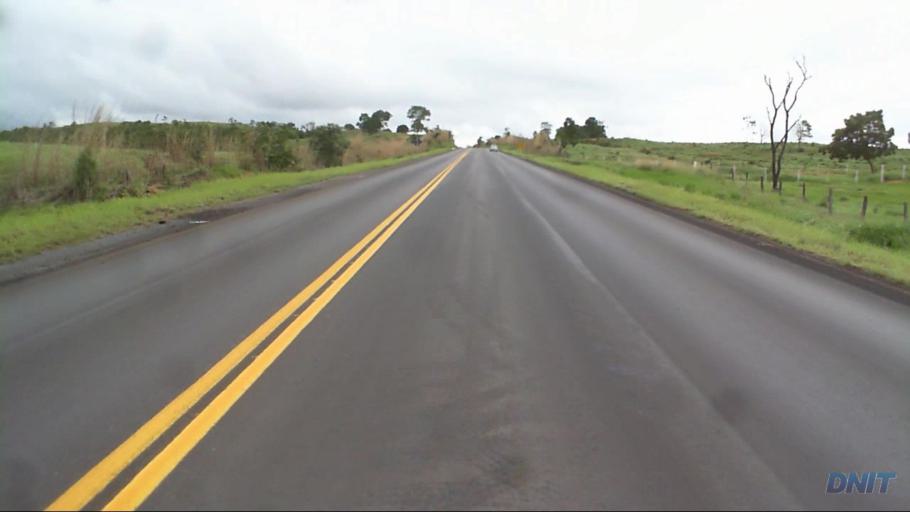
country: BR
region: Goias
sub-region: Padre Bernardo
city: Padre Bernardo
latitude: -15.2200
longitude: -48.5286
